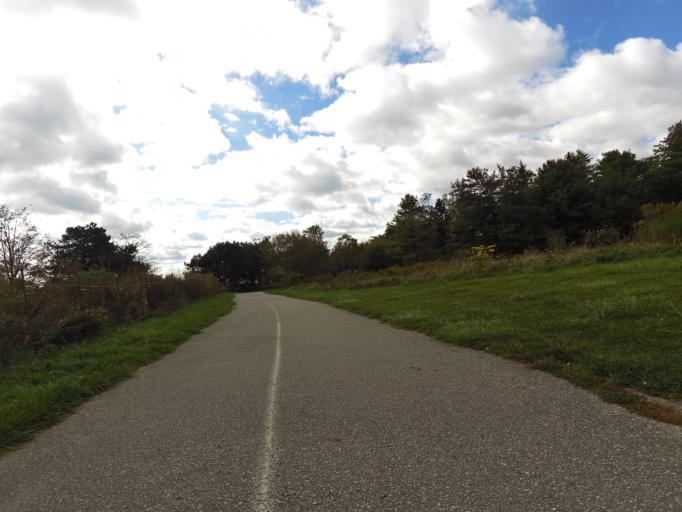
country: CA
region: Ontario
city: Ajax
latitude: 43.7984
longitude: -79.1109
